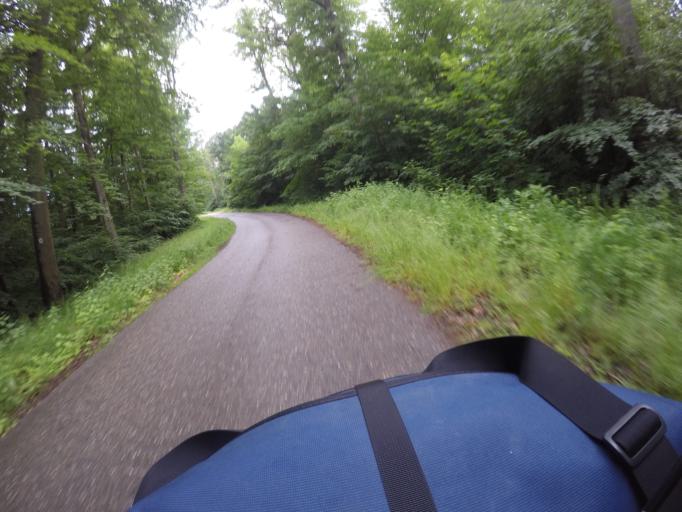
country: DE
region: Baden-Wuerttemberg
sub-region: Regierungsbezirk Stuttgart
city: Gerlingen
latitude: 48.7827
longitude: 9.0748
